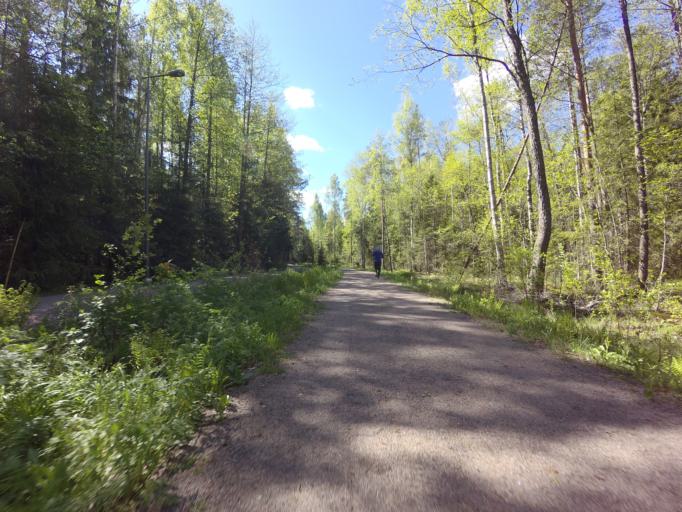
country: FI
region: Uusimaa
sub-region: Helsinki
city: Kauniainen
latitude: 60.1836
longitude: 24.7252
